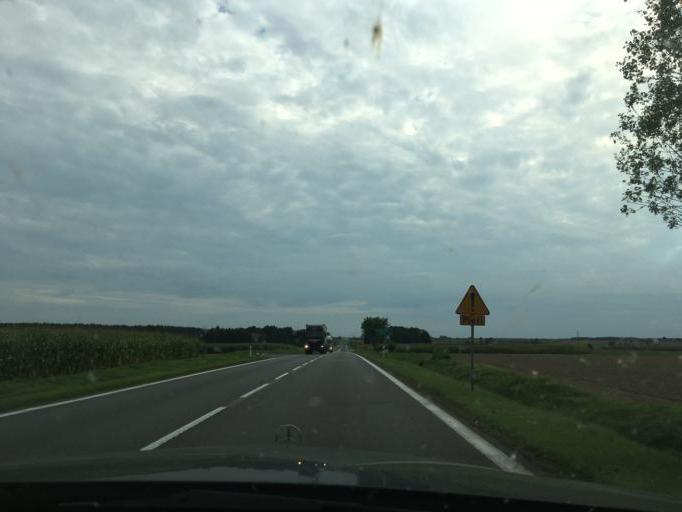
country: PL
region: Podlasie
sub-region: Powiat kolnenski
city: Stawiski
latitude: 53.4220
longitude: 22.1670
